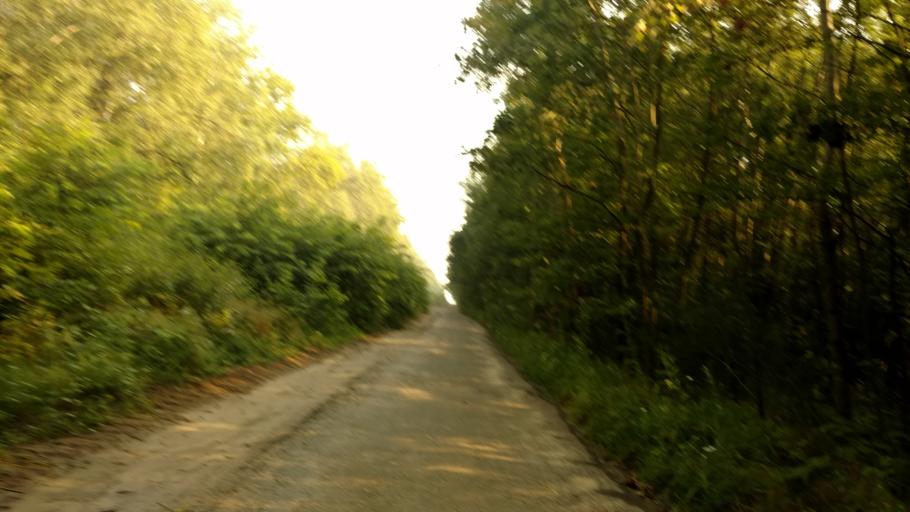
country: PL
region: Silesian Voivodeship
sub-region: Powiat pszczynski
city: Jankowice
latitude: 50.0083
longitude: 18.9739
